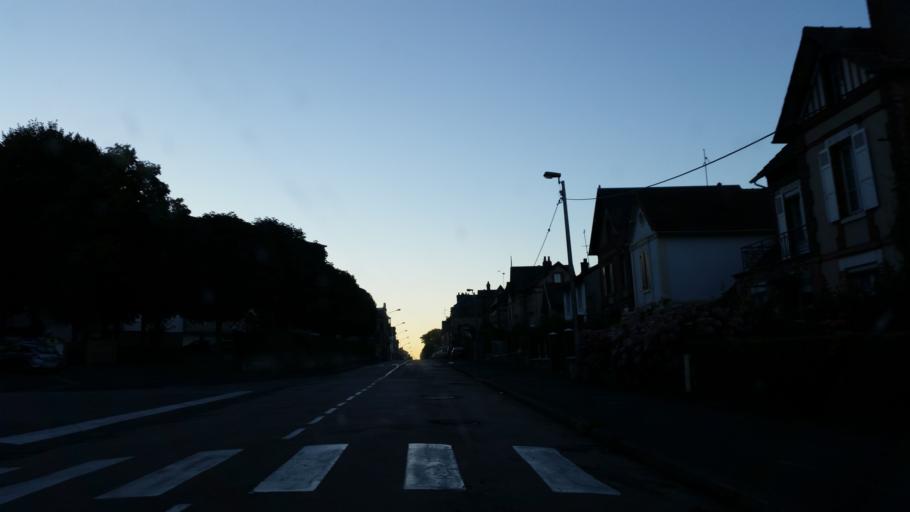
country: FR
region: Lower Normandy
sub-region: Departement du Calvados
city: Honfleur
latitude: 49.4110
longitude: 0.2480
